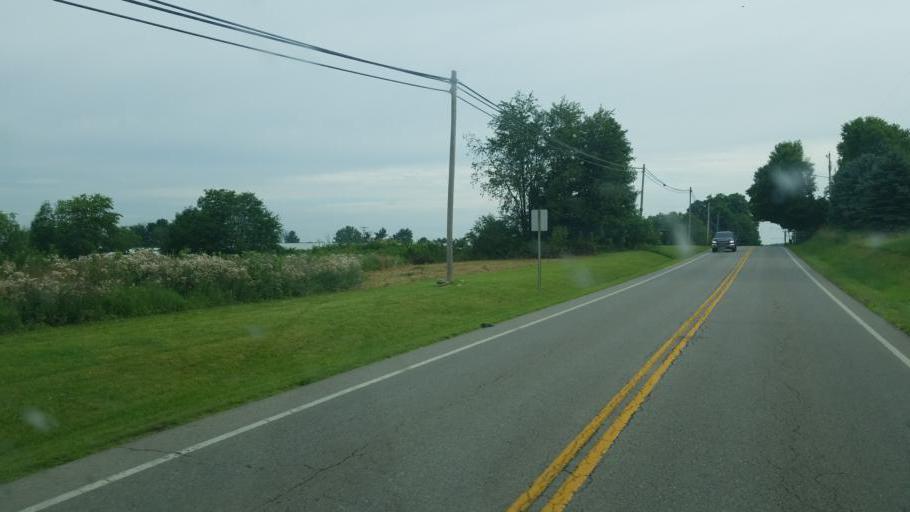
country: US
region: Ohio
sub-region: Sandusky County
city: Bellville
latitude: 40.6073
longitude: -82.5129
